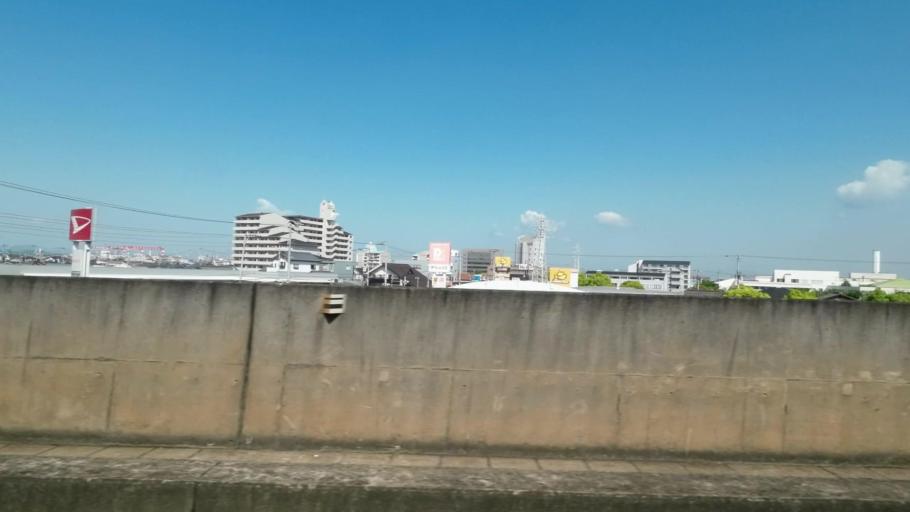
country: JP
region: Kagawa
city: Marugame
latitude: 34.2989
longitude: 133.8091
